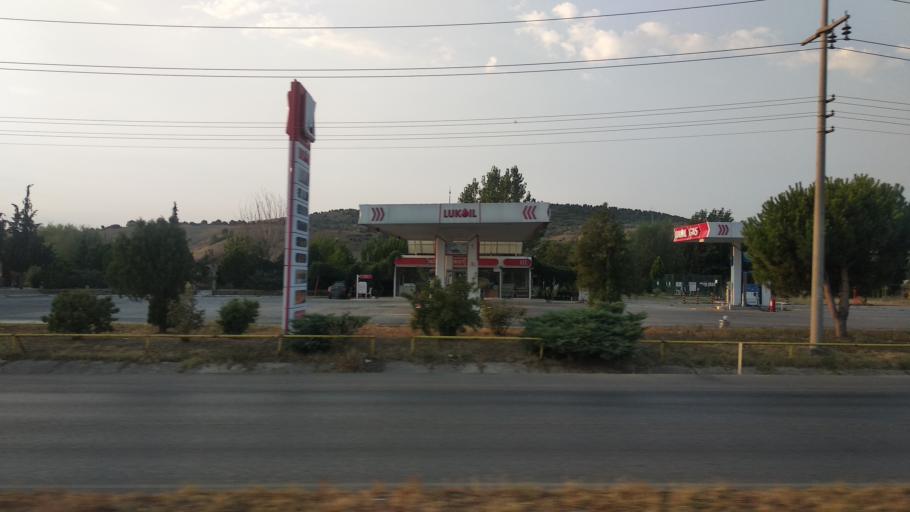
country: TR
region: Manisa
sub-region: Kula
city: Kula
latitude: 38.5446
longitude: 28.6622
